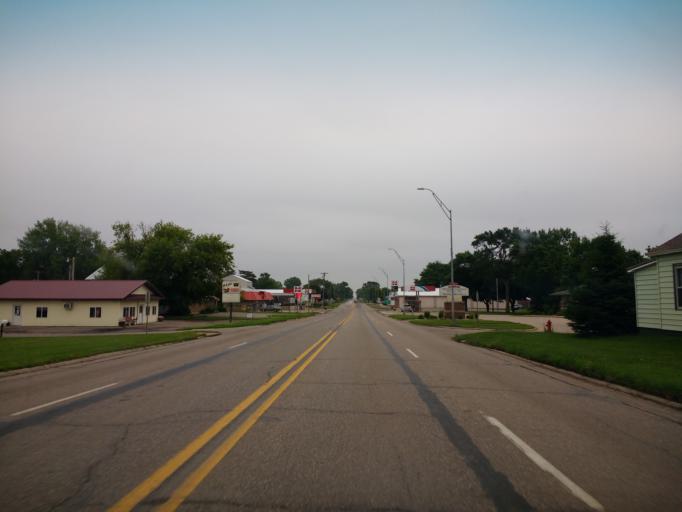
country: US
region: Iowa
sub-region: O'Brien County
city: Hartley
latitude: 43.1848
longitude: -95.4791
